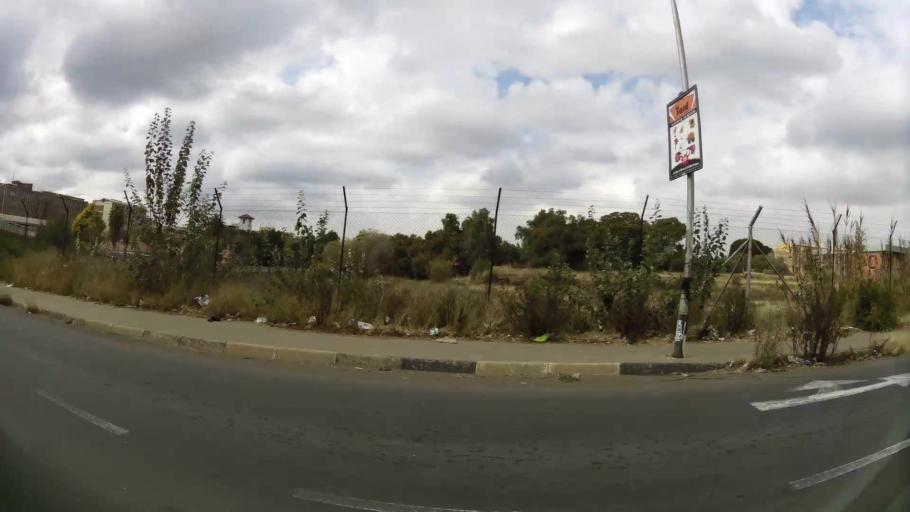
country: ZA
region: Orange Free State
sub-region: Mangaung Metropolitan Municipality
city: Bloemfontein
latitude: -29.1187
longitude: 26.2135
